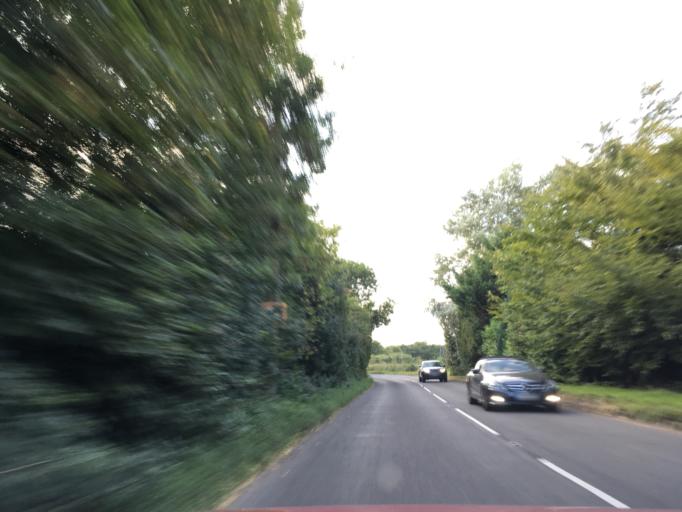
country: GB
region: England
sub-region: Wiltshire
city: Market Lavington
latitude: 51.3212
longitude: -1.9266
